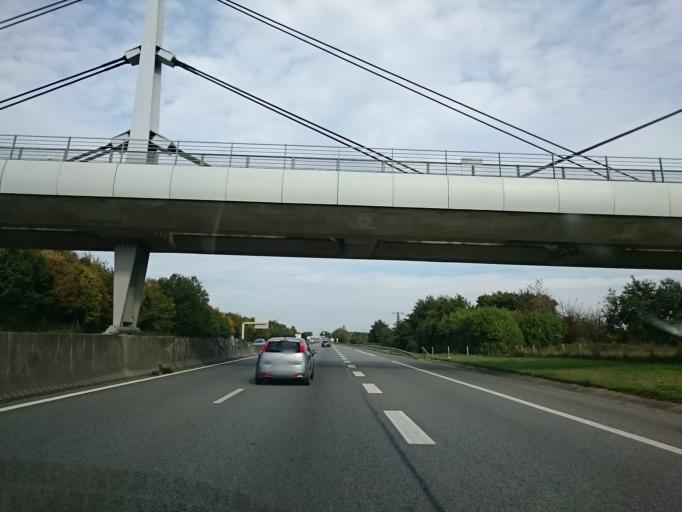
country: FR
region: Brittany
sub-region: Departement d'Ille-et-Vilaine
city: Chantepie
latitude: 48.0844
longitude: -1.6410
